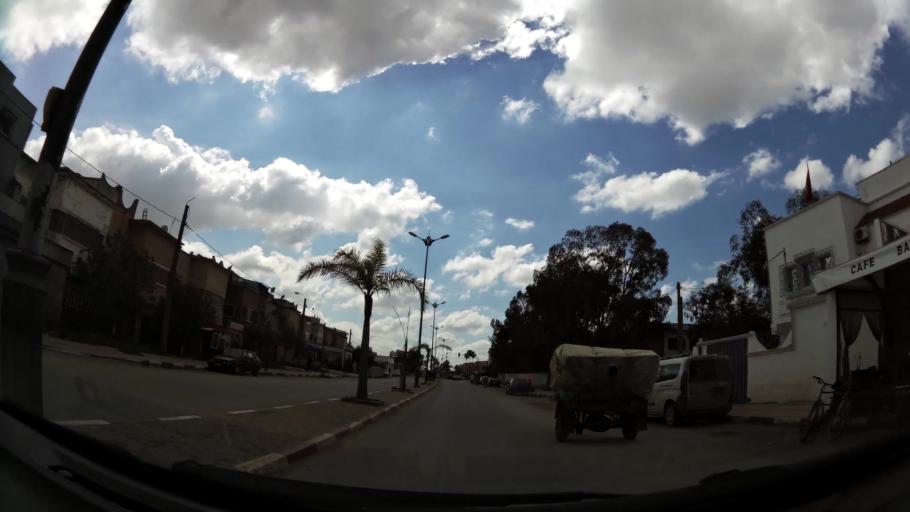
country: MA
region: Grand Casablanca
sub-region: Mediouna
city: Mediouna
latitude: 33.3732
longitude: -7.5323
